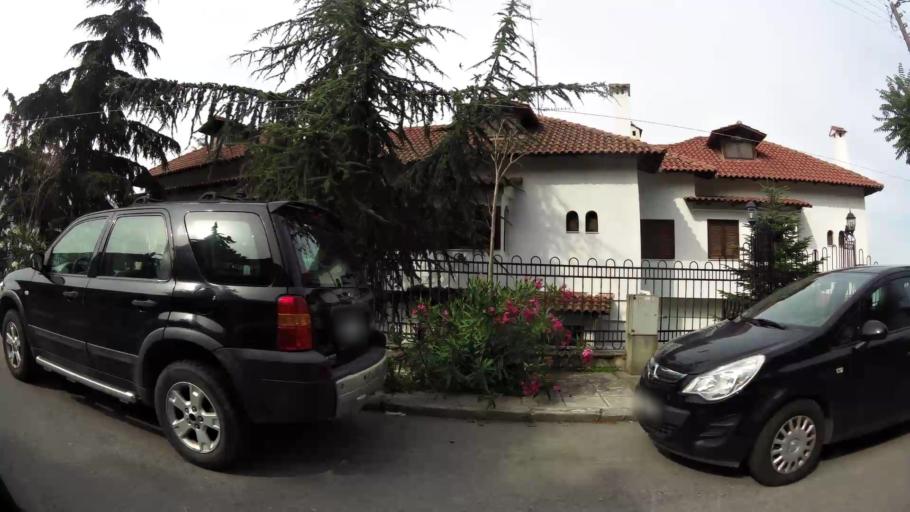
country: GR
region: Central Macedonia
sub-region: Nomos Thessalonikis
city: Panorama
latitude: 40.5860
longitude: 23.0281
